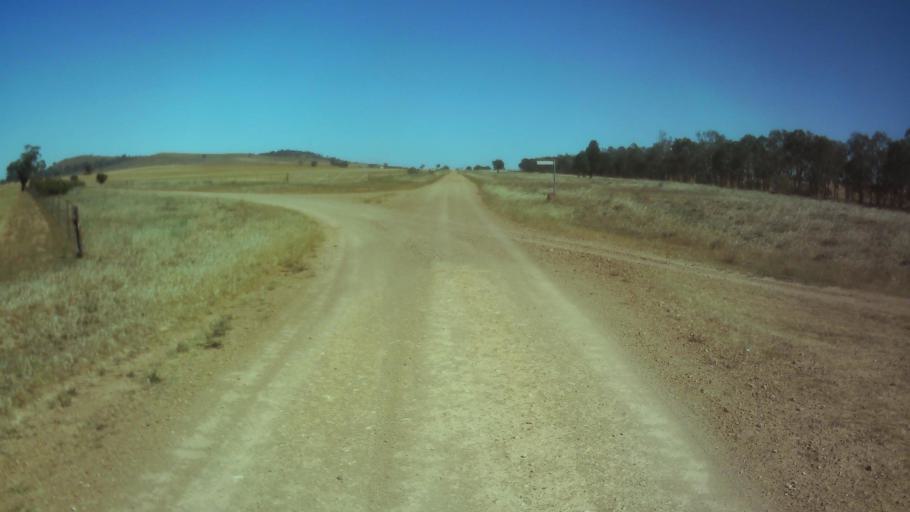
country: AU
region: New South Wales
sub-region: Weddin
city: Grenfell
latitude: -33.9707
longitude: 148.3164
